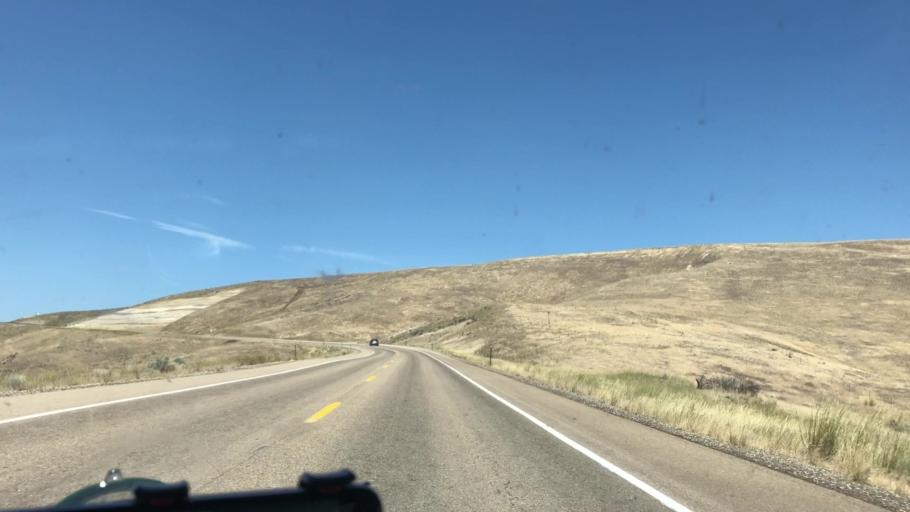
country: US
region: Idaho
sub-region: Owyhee County
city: Marsing
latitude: 43.2852
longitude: -116.9883
